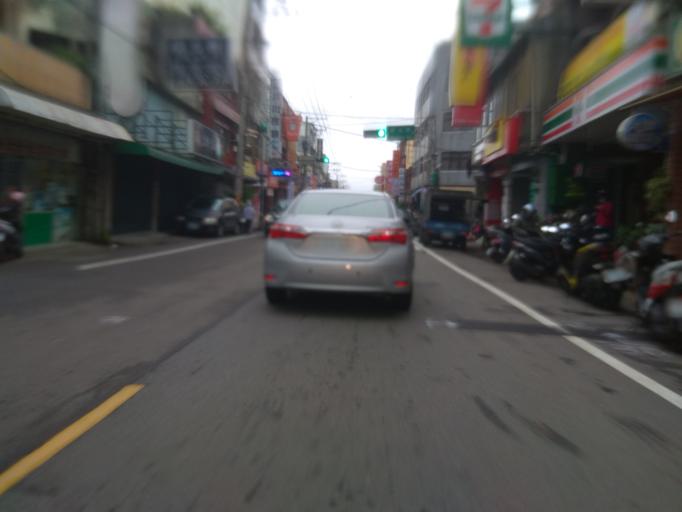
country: TW
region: Taiwan
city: Taoyuan City
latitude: 25.0128
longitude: 121.1362
